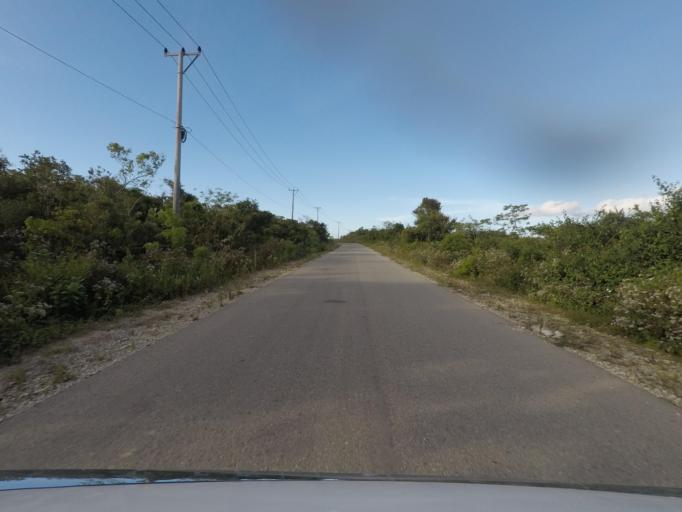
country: TL
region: Lautem
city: Lospalos
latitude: -8.4028
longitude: 127.0021
